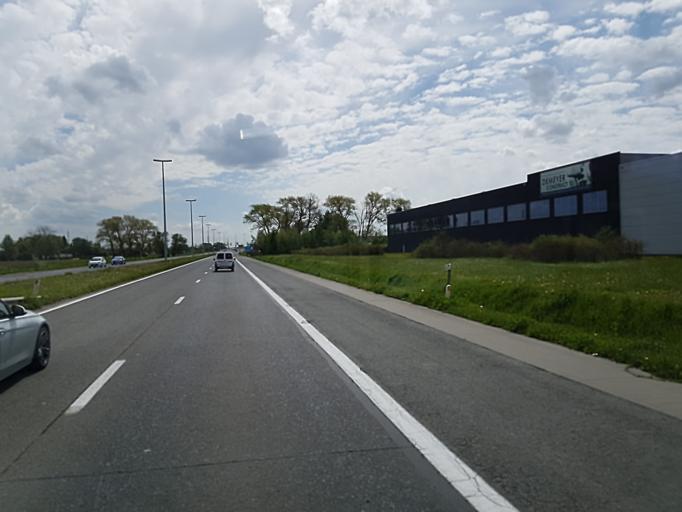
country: BE
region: Flanders
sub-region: Provincie West-Vlaanderen
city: Menen
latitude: 50.8146
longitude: 3.1291
